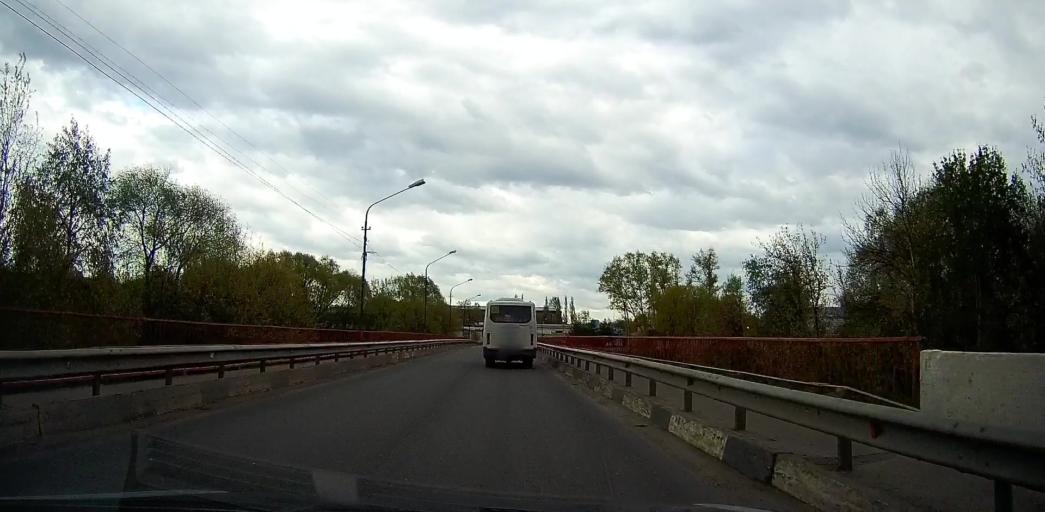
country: RU
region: Moskovskaya
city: Pavlovskiy Posad
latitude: 55.7804
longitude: 38.6878
